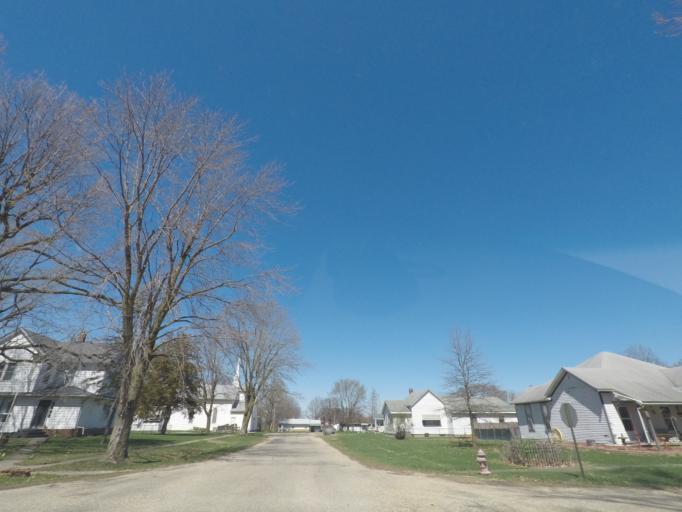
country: US
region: Illinois
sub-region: Macon County
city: Warrensburg
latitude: 39.9674
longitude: -89.1616
